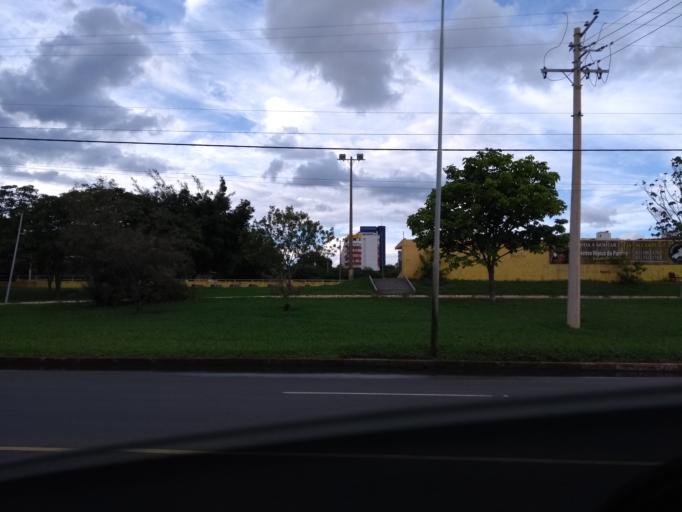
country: BR
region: Federal District
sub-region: Brasilia
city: Brasilia
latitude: -15.8048
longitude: -47.9212
